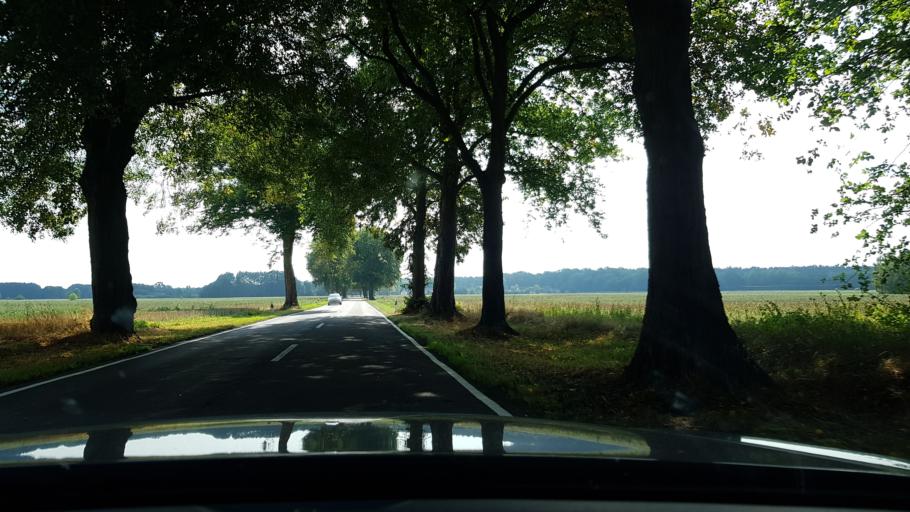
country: DE
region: Brandenburg
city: Lindow
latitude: 53.0000
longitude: 12.9740
